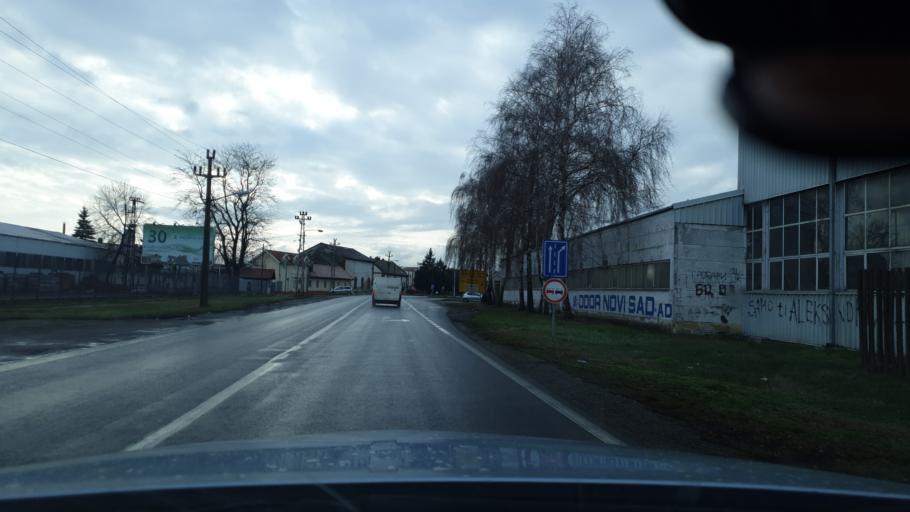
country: RS
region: Autonomna Pokrajina Vojvodina
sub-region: Juznobanatski Okrug
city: Kovin
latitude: 44.7543
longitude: 20.9671
